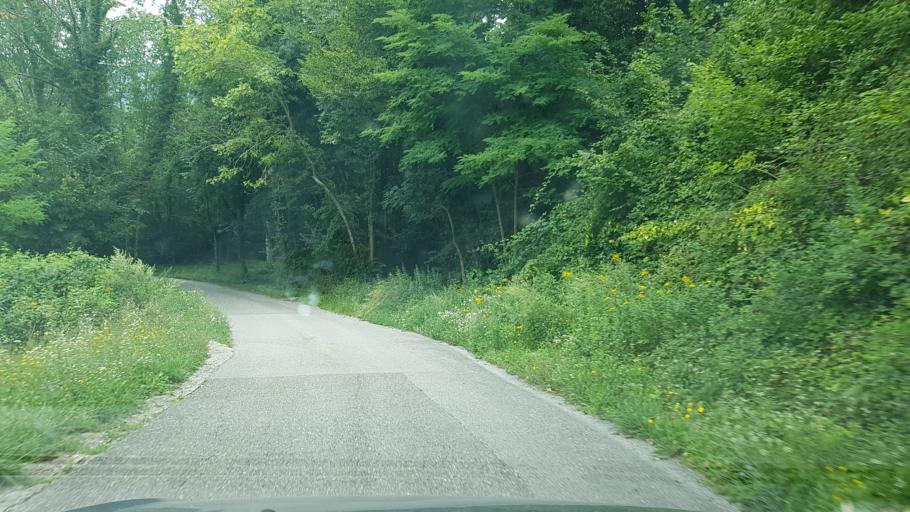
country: SI
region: Kanal
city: Deskle
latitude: 46.0296
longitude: 13.6011
